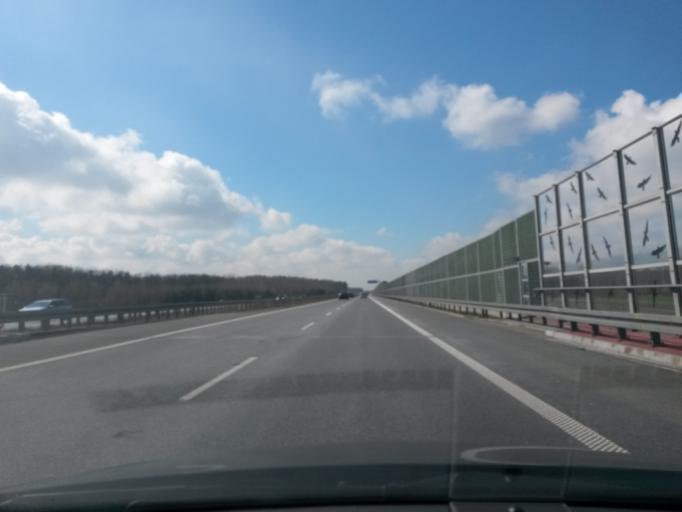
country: PL
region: Lodz Voivodeship
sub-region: powiat Lowicki
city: Nieborow
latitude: 52.0508
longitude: 20.1004
